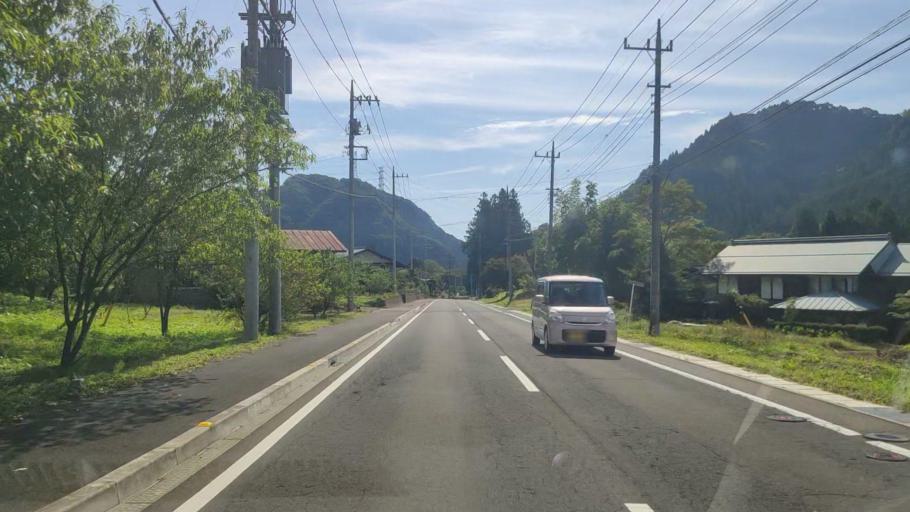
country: JP
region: Gunma
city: Nakanojomachi
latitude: 36.6110
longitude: 138.7871
